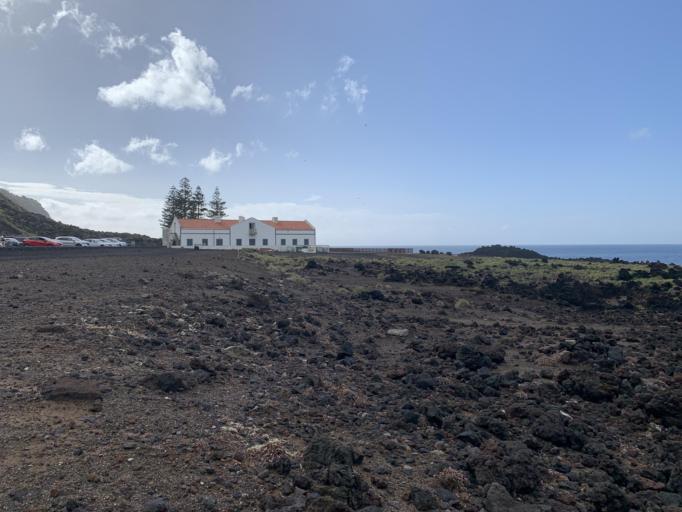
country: PT
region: Azores
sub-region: Ponta Delgada
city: Arrifes
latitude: 37.8619
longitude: -25.8520
